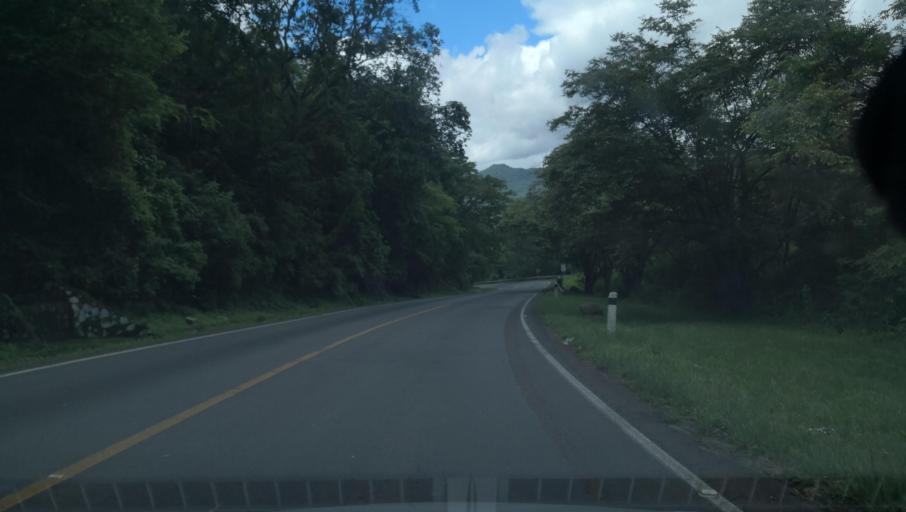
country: NI
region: Esteli
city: Condega
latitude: 13.2499
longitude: -86.3591
